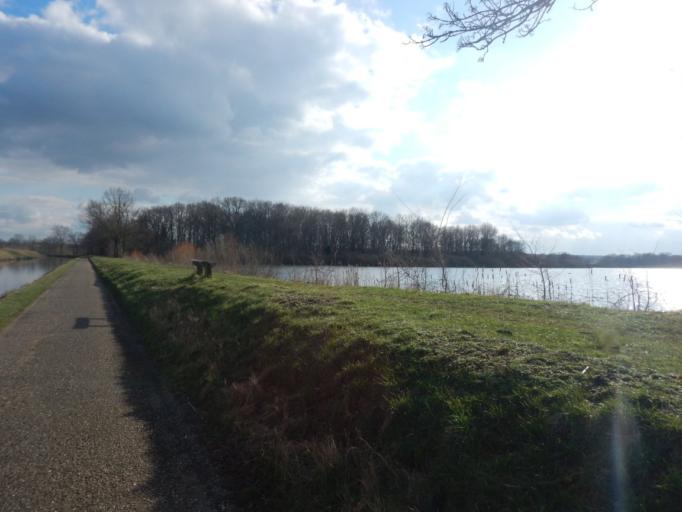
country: FR
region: Lorraine
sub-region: Departement de la Moselle
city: Lorquin
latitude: 48.6990
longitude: 6.9098
